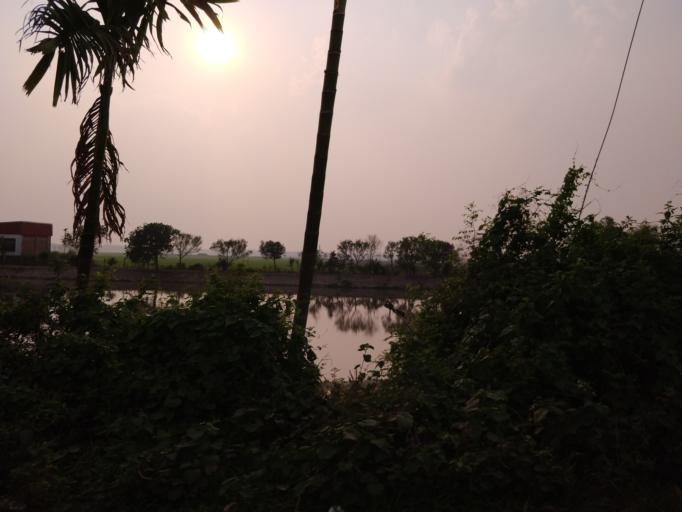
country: BD
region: Sylhet
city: Habiganj
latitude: 24.1365
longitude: 91.3516
